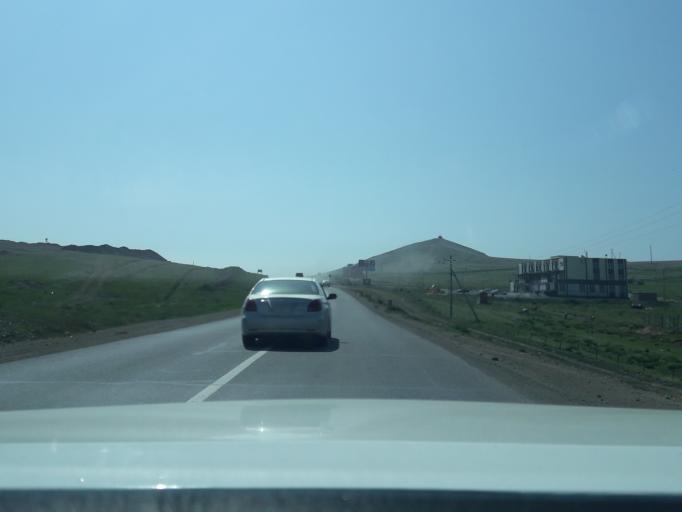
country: MN
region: Ulaanbaatar
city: Ulaanbaatar
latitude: 47.7920
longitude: 106.7455
